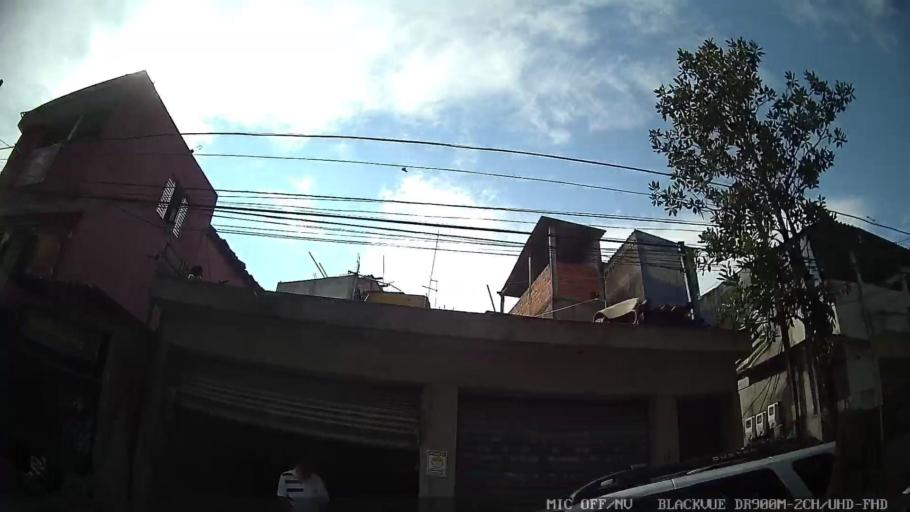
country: BR
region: Sao Paulo
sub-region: Ferraz De Vasconcelos
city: Ferraz de Vasconcelos
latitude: -23.5319
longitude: -46.4169
